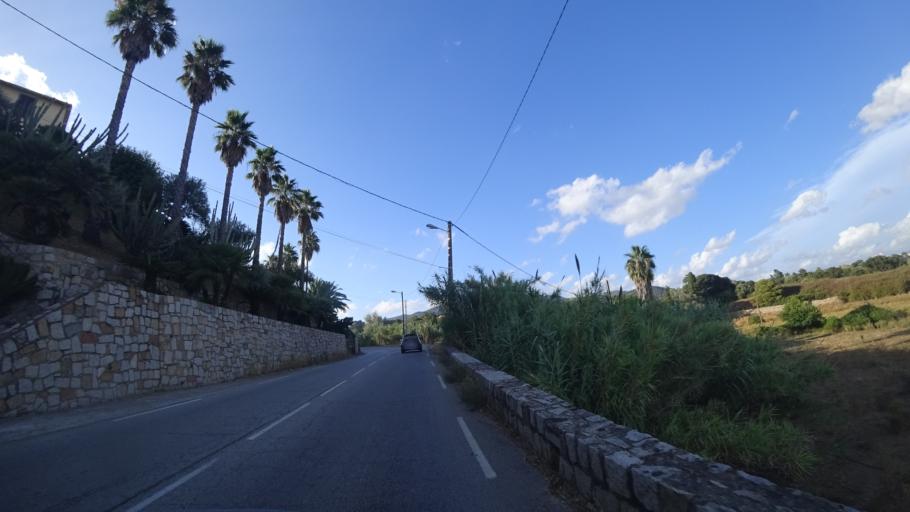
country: FR
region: Corsica
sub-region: Departement de la Corse-du-Sud
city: Ajaccio
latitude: 41.9395
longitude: 8.7382
